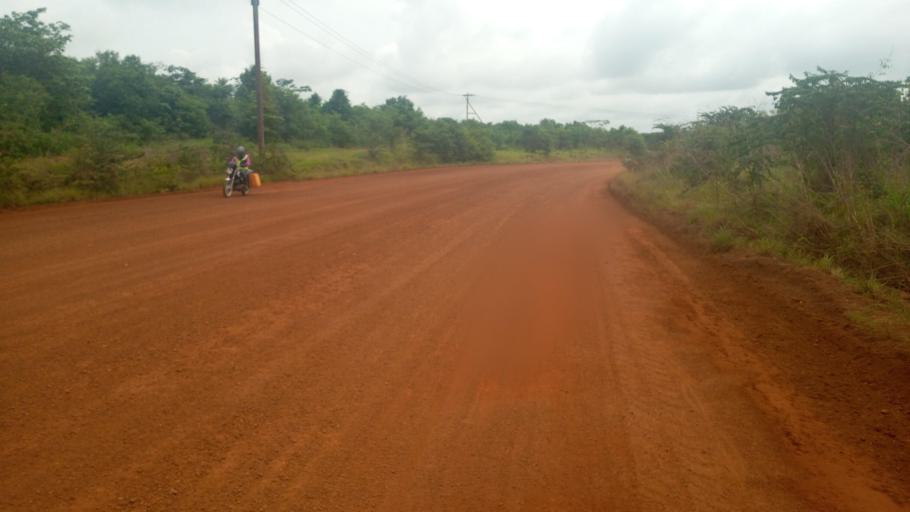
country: SL
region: Southern Province
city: Mogbwemo
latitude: 7.7203
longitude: -12.2857
